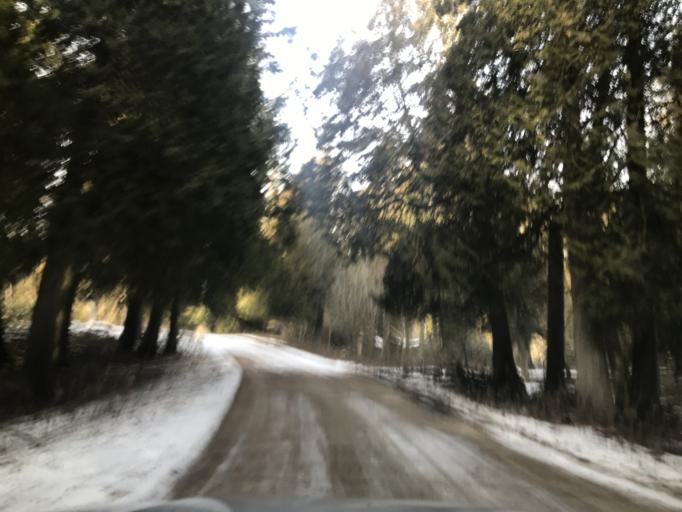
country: US
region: Wisconsin
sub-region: Door County
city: Sturgeon Bay
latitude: 45.1476
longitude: -87.0320
